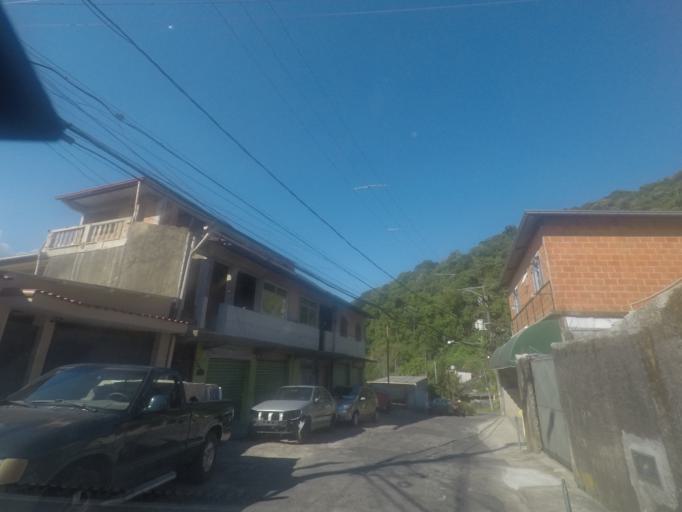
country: BR
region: Rio de Janeiro
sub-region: Petropolis
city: Petropolis
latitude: -22.5444
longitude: -43.2031
